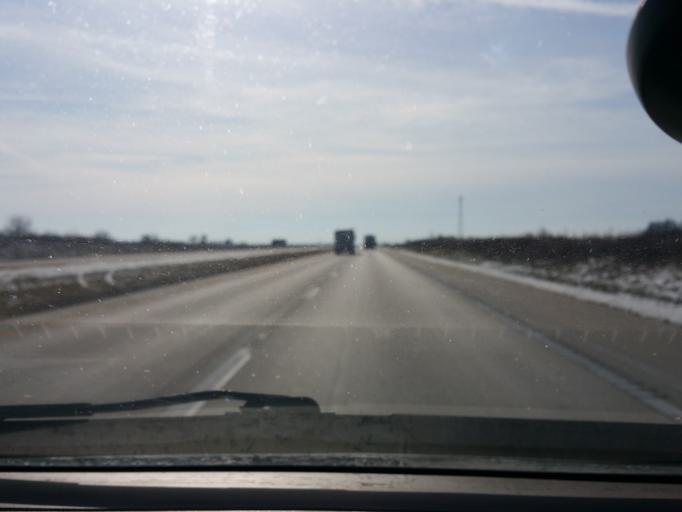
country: US
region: Missouri
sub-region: Clinton County
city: Lathrop
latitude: 39.5823
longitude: -94.2589
